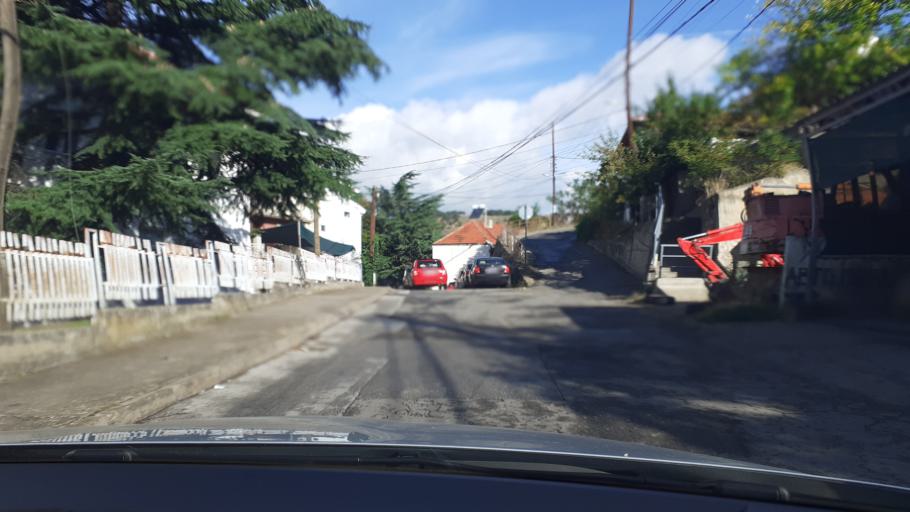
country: MK
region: Kocani
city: Kochani
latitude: 41.9213
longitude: 22.4117
